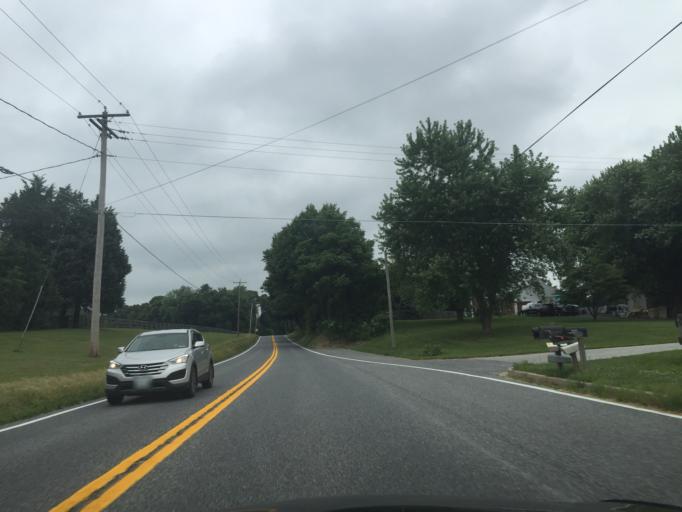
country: US
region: Maryland
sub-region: Harford County
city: Jarrettsville
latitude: 39.6064
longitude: -76.5133
